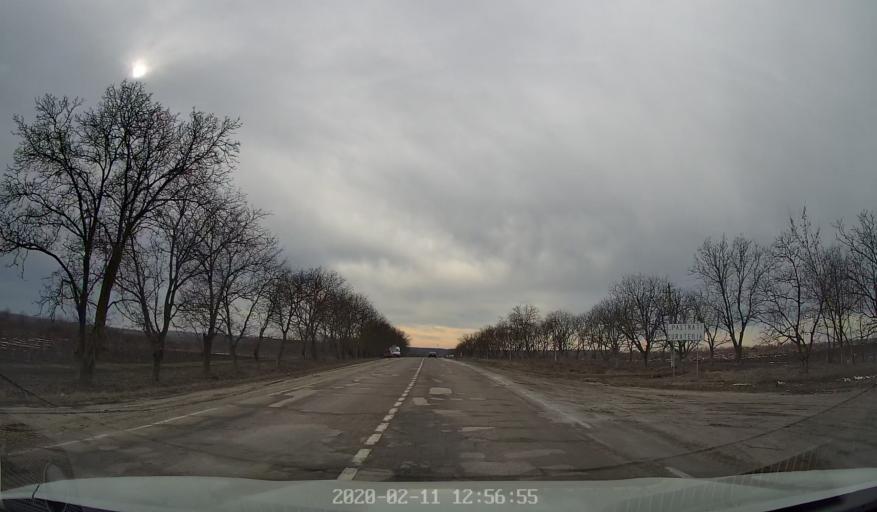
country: MD
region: Briceni
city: Briceni
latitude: 48.3460
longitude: 27.0736
